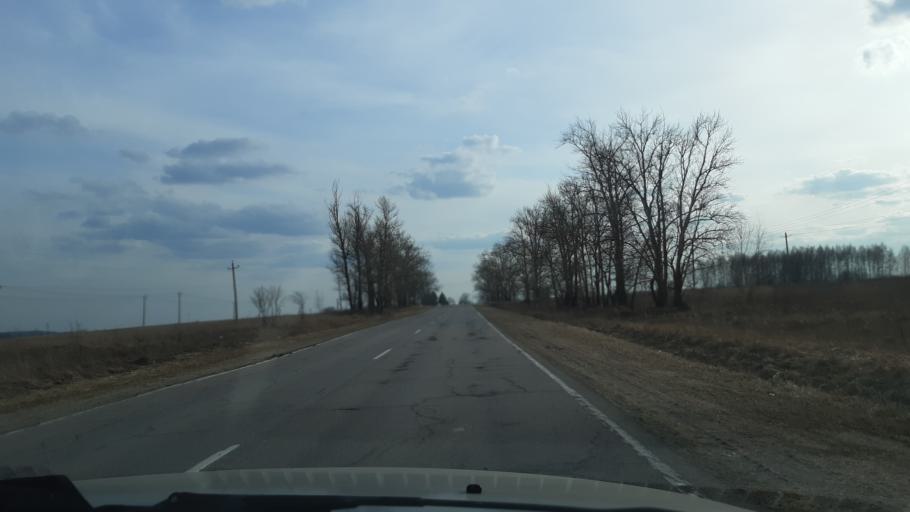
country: RU
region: Vladimir
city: Nikologory
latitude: 56.1660
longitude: 41.9980
